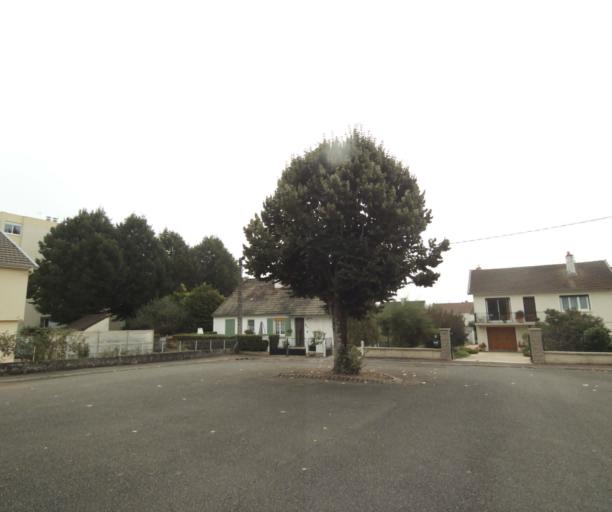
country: FR
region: Bourgogne
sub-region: Departement de Saone-et-Loire
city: Charolles
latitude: 46.4328
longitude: 4.2655
